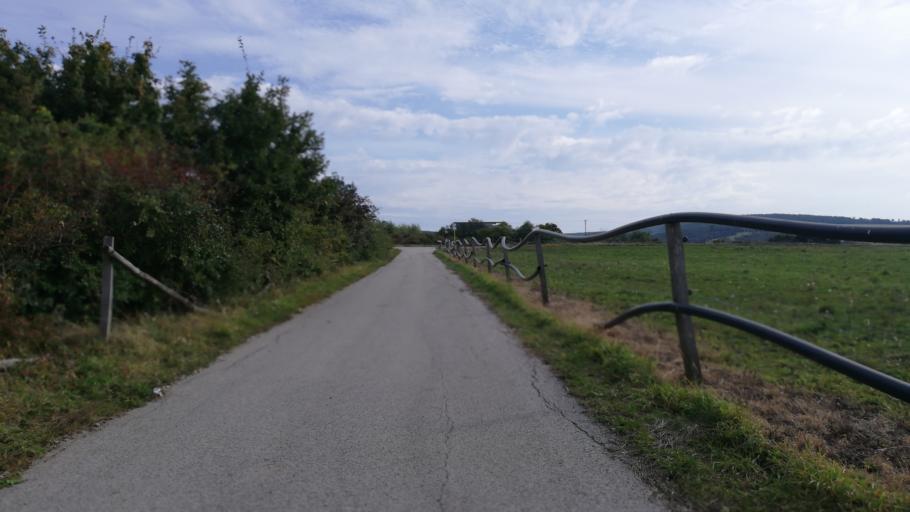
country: CZ
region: South Moravian
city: Sudomerice
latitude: 48.8400
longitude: 17.2845
